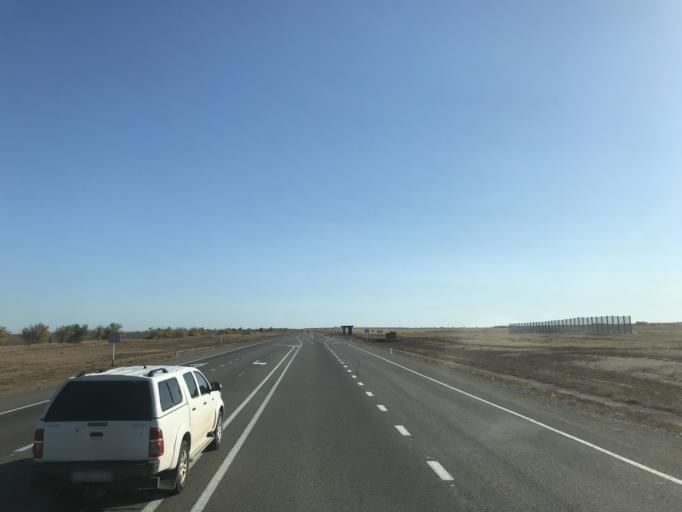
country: KZ
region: Pavlodar
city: Koktobe
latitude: 51.8136
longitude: 77.4715
